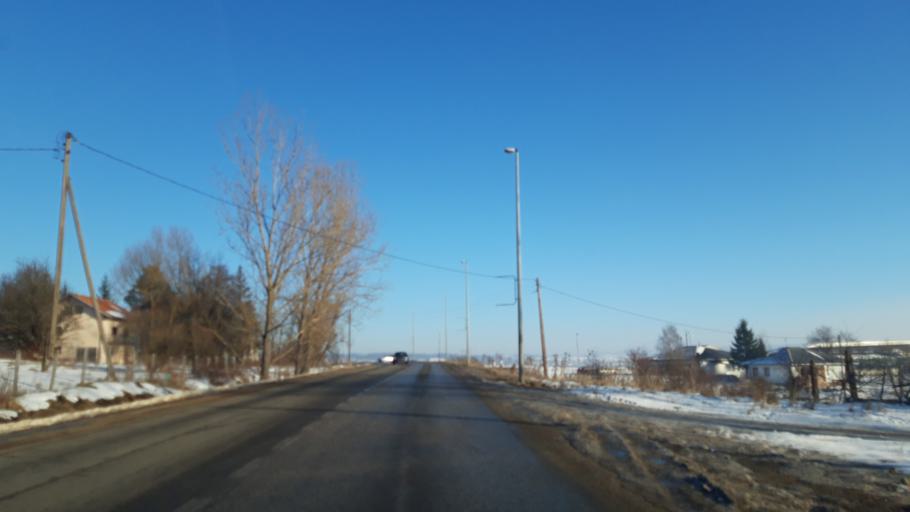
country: BA
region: Republika Srpska
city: Sokolac
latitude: 43.9228
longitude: 18.7777
